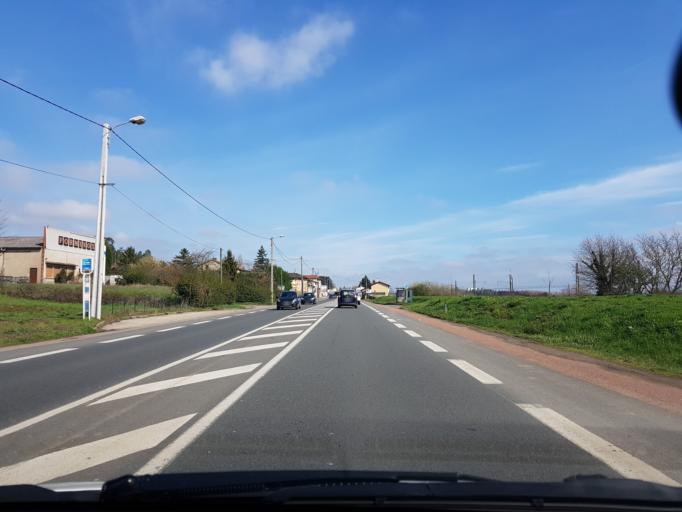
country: FR
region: Rhone-Alpes
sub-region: Departement du Rhone
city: Villefranche-sur-Saone
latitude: 45.9630
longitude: 4.7159
